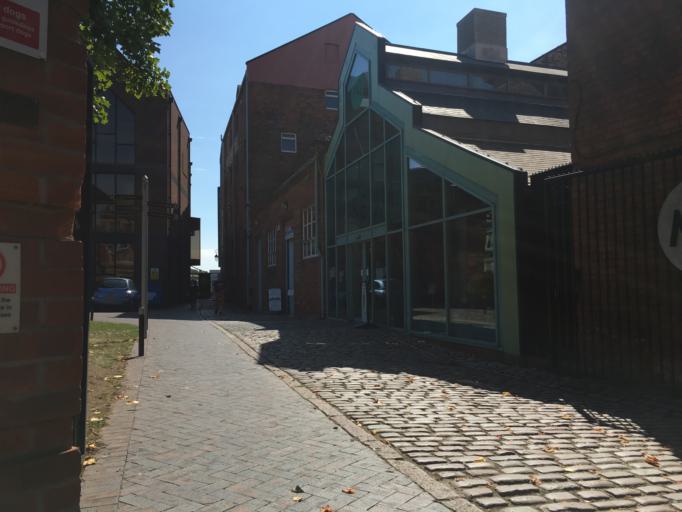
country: GB
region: England
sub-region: City of Kingston upon Hull
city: Hull
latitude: 53.7437
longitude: -0.3306
